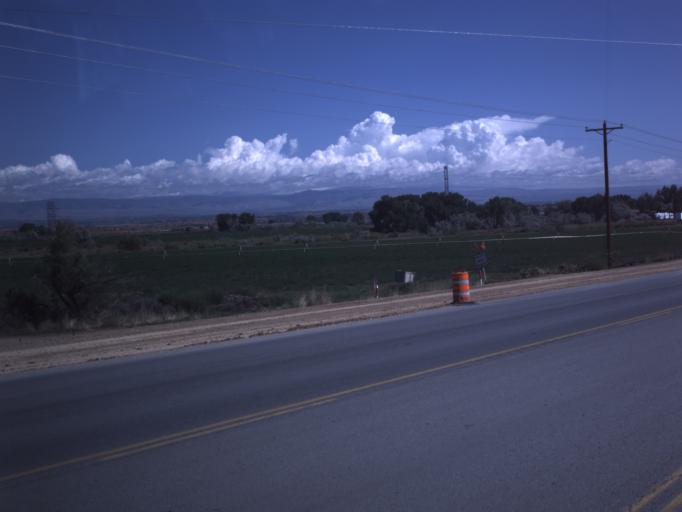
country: US
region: Utah
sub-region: Duchesne County
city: Roosevelt
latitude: 40.2583
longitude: -110.0605
